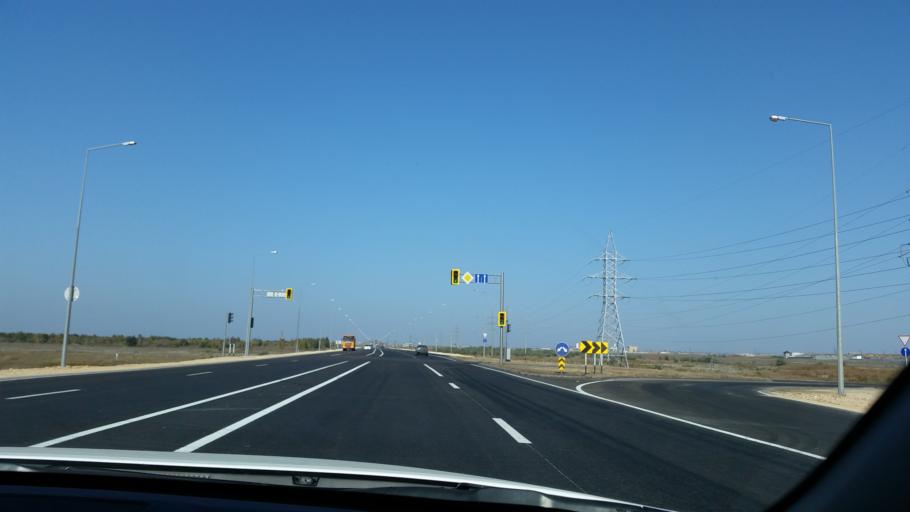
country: KZ
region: Astana Qalasy
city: Astana
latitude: 51.2090
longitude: 71.3142
